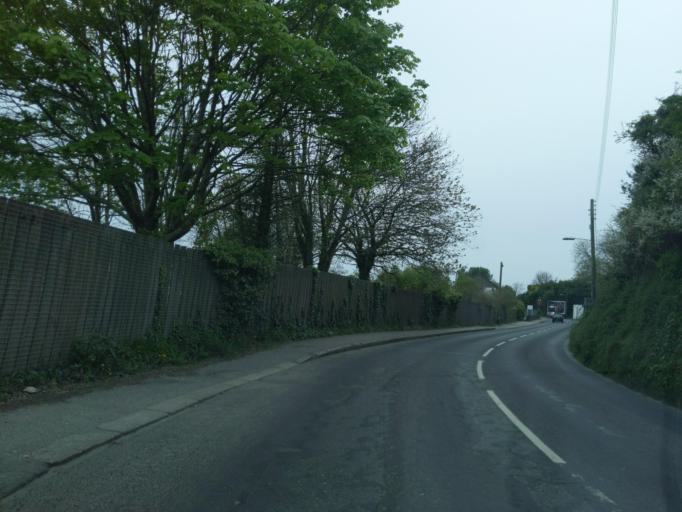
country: GB
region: England
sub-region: Cornwall
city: Par
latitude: 50.3482
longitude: -4.7059
